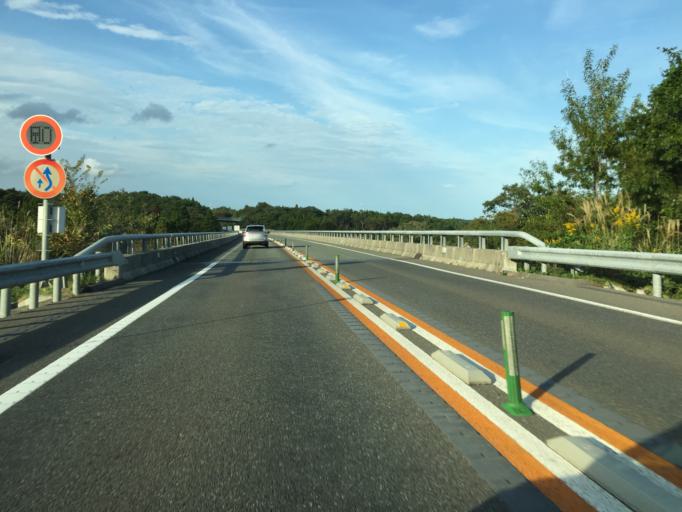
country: JP
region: Fukushima
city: Iwaki
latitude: 37.2484
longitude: 140.9892
